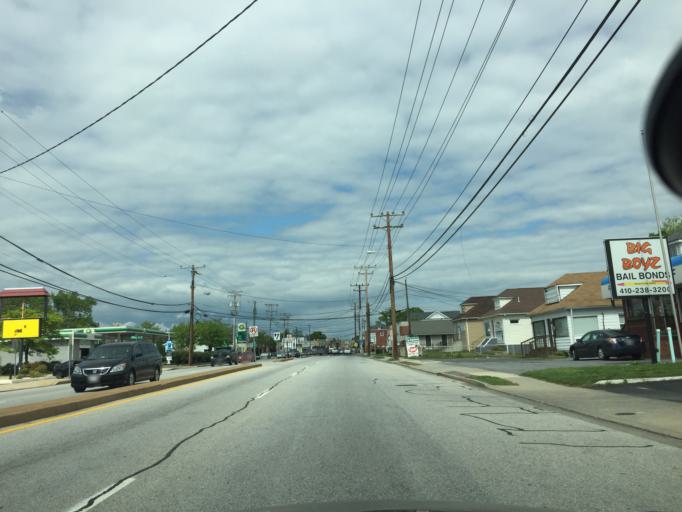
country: US
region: Maryland
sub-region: Baltimore County
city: Essex
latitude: 39.3056
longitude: -76.4818
